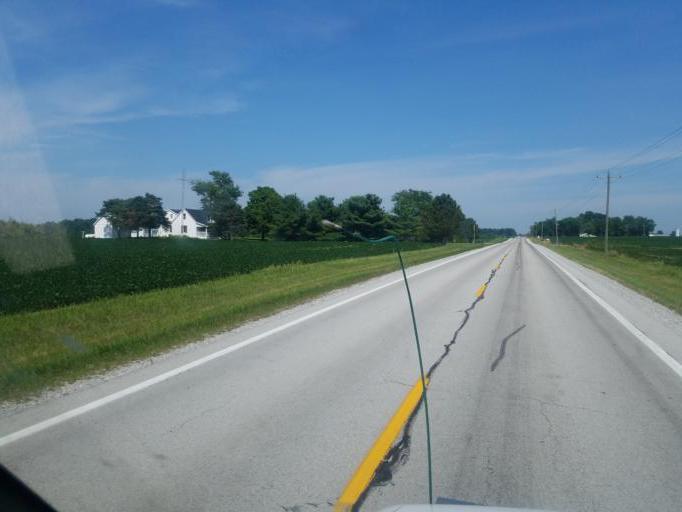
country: US
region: Ohio
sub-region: Shelby County
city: Botkins
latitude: 40.4964
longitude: -84.2749
